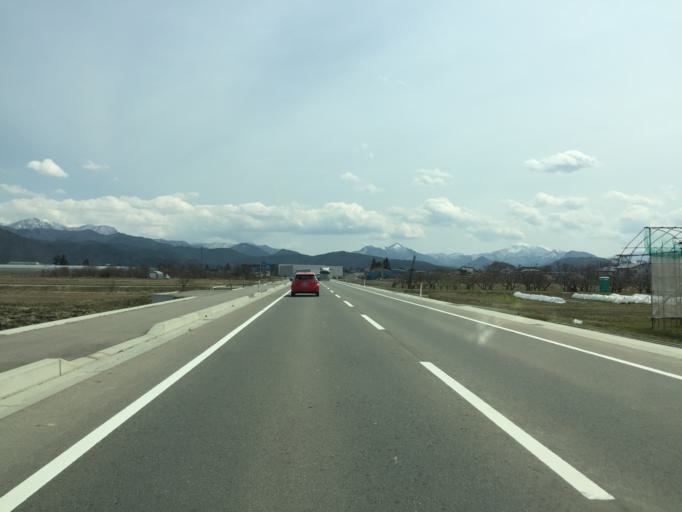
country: JP
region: Yamagata
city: Higashine
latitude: 38.4492
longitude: 140.3744
